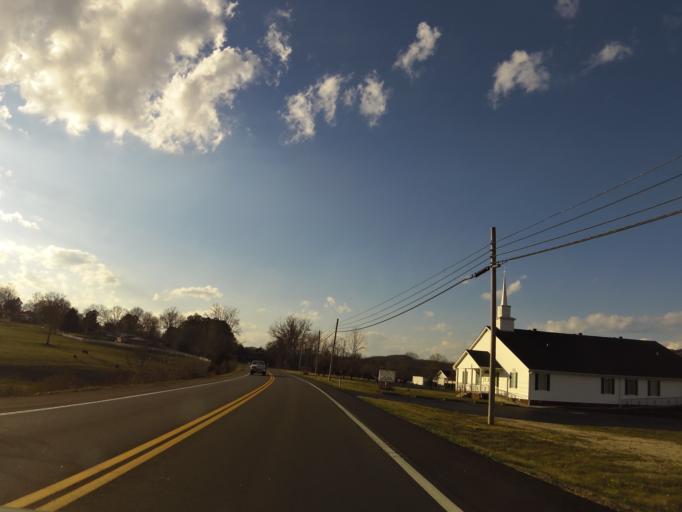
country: US
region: Tennessee
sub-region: Smith County
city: Carthage
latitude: 36.2561
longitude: -85.9617
